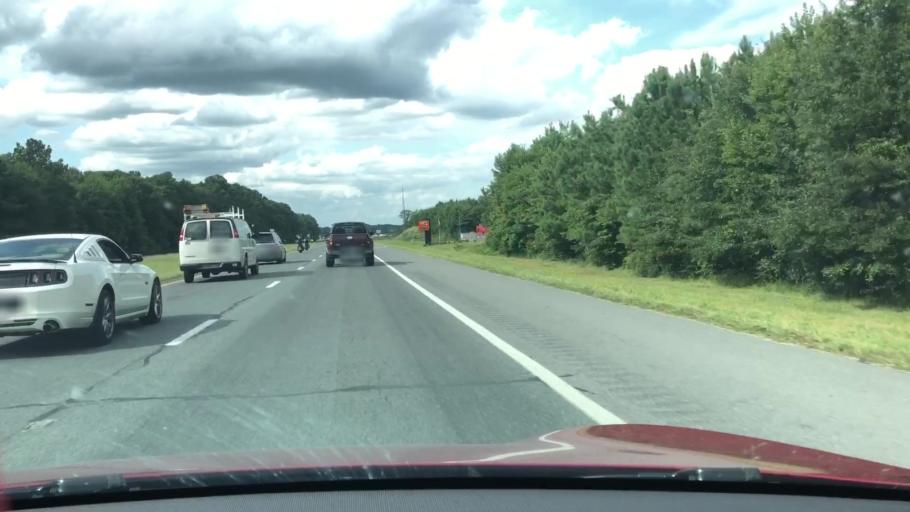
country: US
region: Delaware
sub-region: Sussex County
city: Delmar
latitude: 38.4888
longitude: -75.5566
